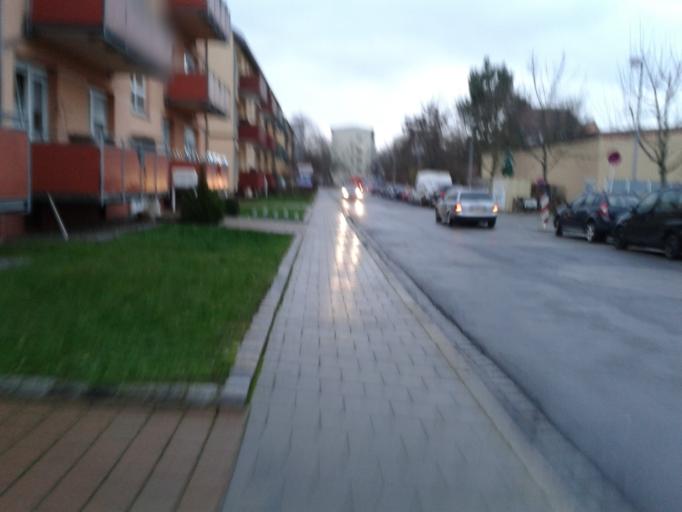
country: DE
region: Bavaria
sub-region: Upper Franconia
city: Bamberg
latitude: 49.9117
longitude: 10.9084
